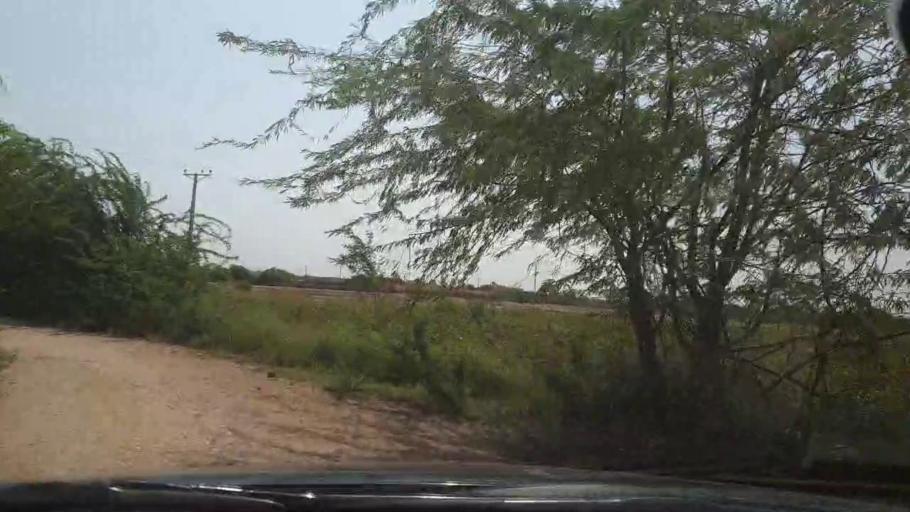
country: PK
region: Sindh
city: Tando Bago
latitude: 24.8021
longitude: 69.1545
